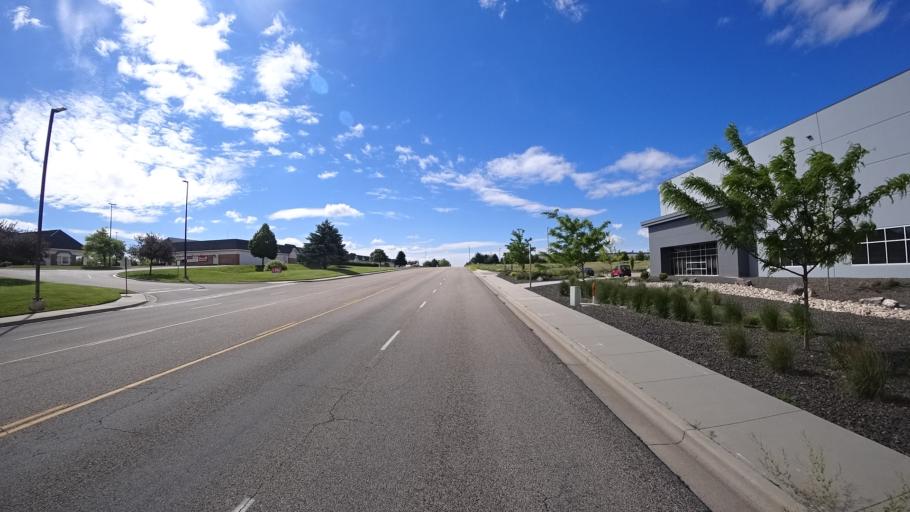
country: US
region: Idaho
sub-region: Ada County
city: Boise
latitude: 43.5401
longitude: -116.1641
